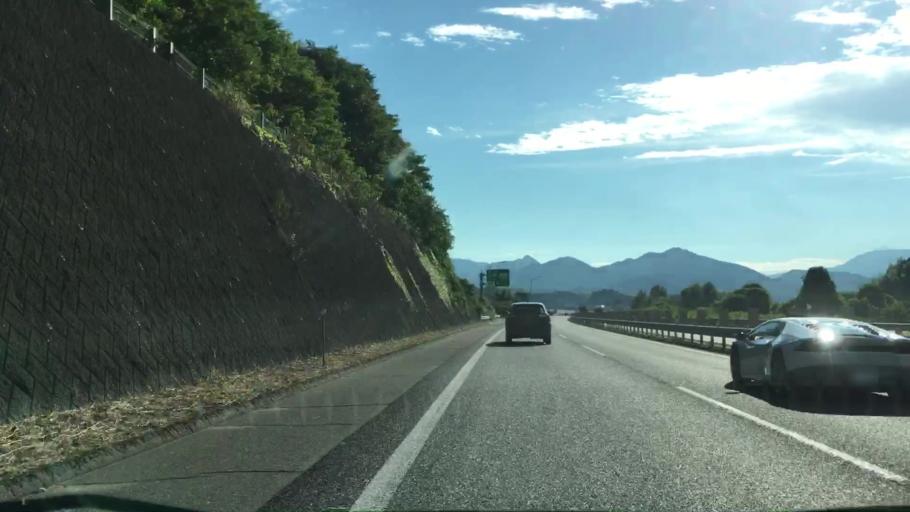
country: JP
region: Yamaguchi
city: Yanai
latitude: 34.0839
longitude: 132.0855
